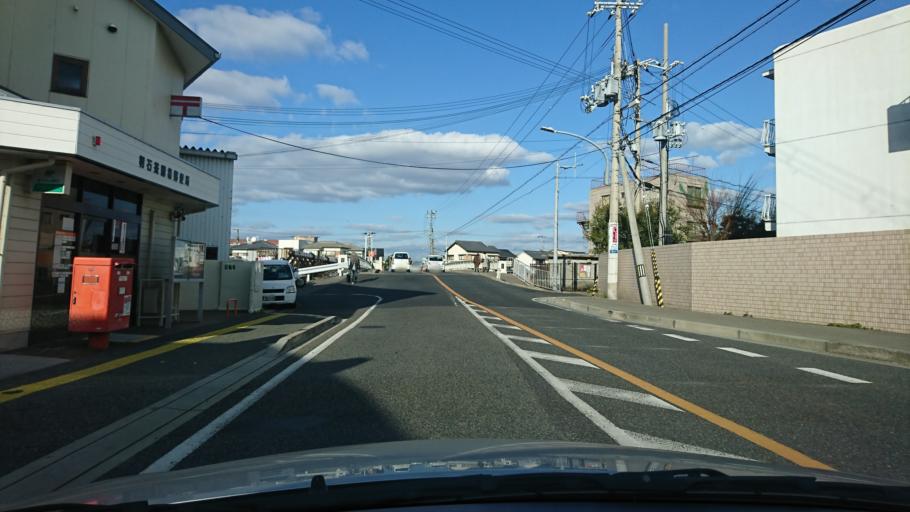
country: JP
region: Hyogo
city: Akashi
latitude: 34.6575
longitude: 134.9895
